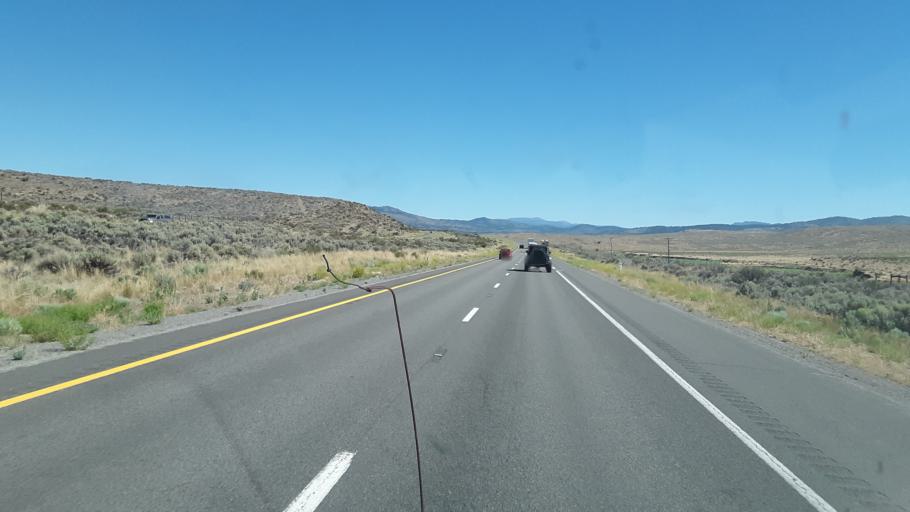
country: US
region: Nevada
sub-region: Washoe County
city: Cold Springs
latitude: 39.7077
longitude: -120.0351
